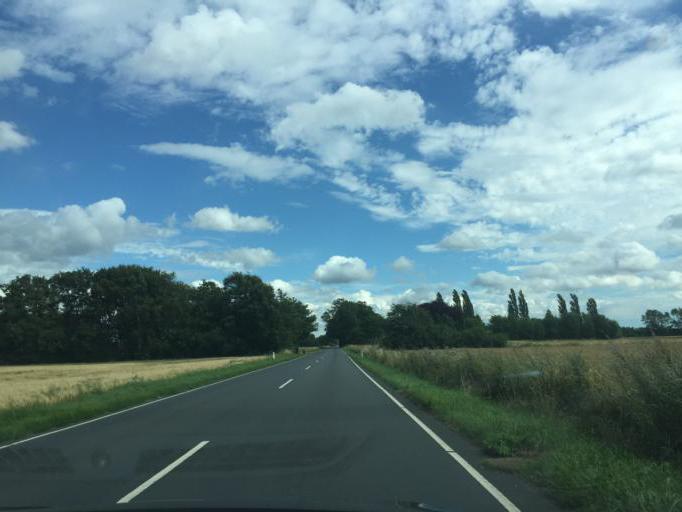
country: DK
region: South Denmark
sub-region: Nordfyns Kommune
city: Otterup
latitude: 55.4847
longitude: 10.3717
